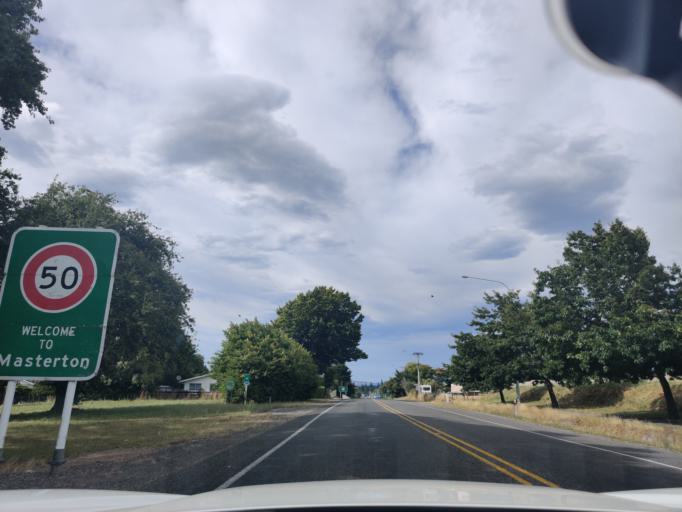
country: NZ
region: Wellington
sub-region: Masterton District
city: Masterton
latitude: -40.9354
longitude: 175.6711
